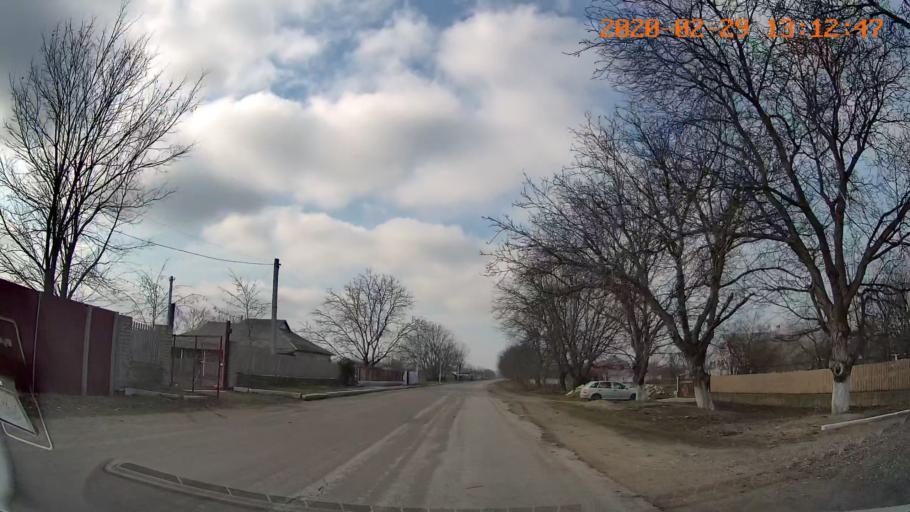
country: MD
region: Telenesti
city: Camenca
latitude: 48.0133
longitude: 28.6918
